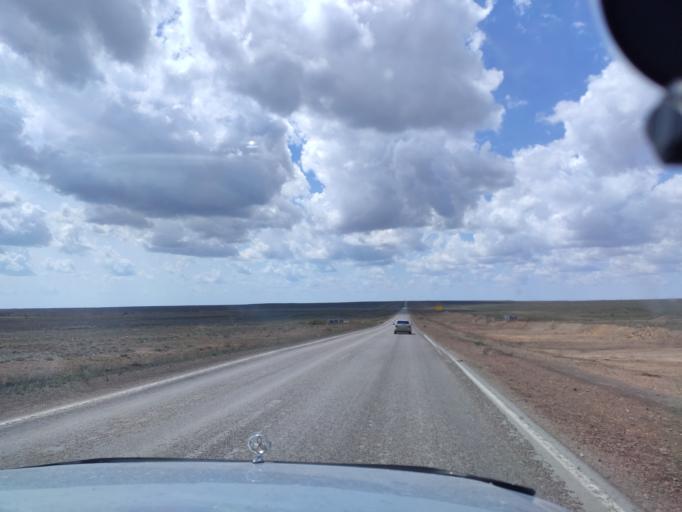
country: KZ
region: Qaraghandy
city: Saryshaghan
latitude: 46.0026
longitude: 73.5813
